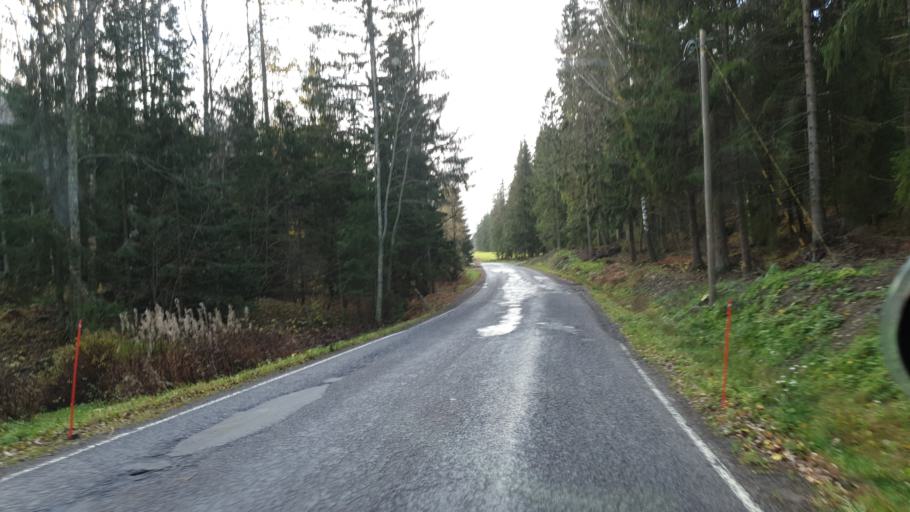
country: FI
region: Uusimaa
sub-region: Helsinki
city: Siuntio
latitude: 60.2649
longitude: 24.3038
